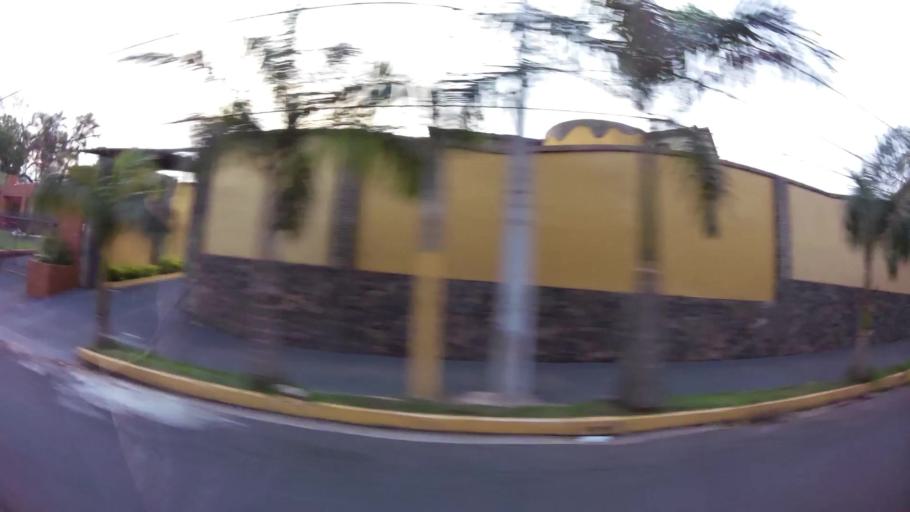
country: PY
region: Central
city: Lambare
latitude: -25.3373
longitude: -57.6224
